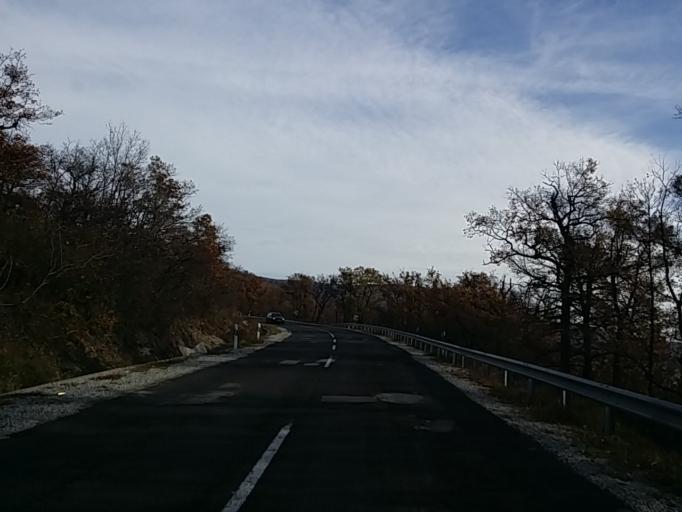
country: HU
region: Heves
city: Gyongyossolymos
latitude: 47.8406
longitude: 19.9599
